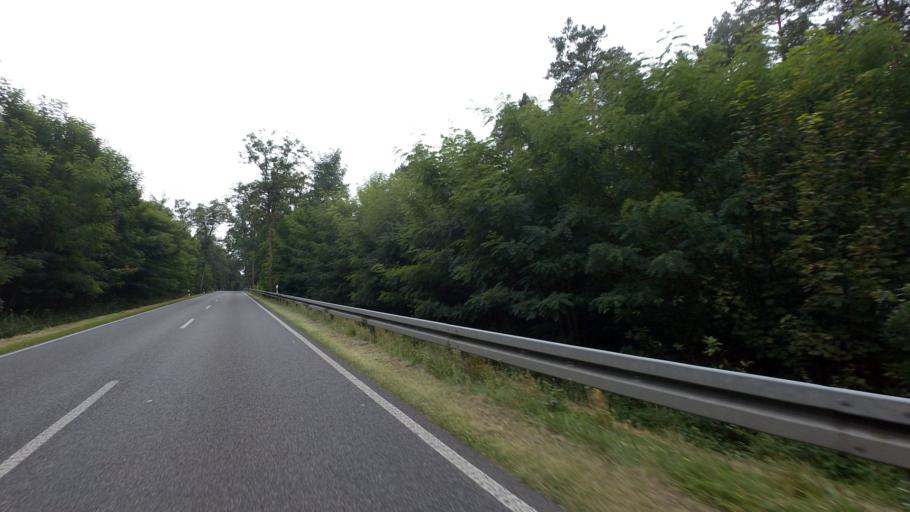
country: DE
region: Brandenburg
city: Baruth
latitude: 52.0947
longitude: 13.4959
